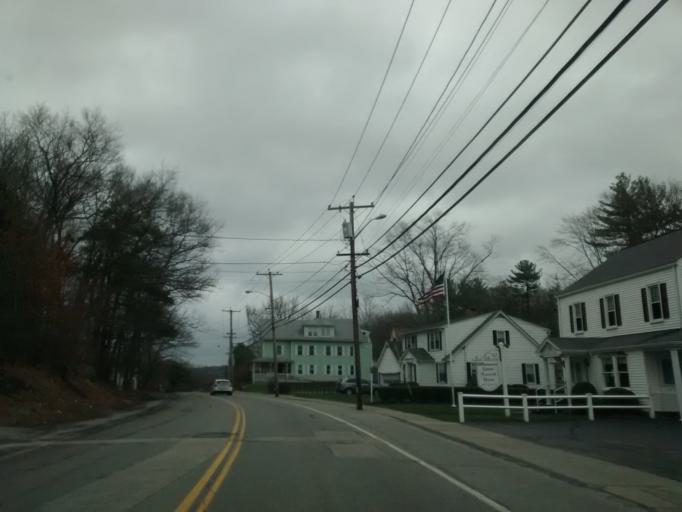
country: US
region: Massachusetts
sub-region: Worcester County
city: Whitinsville
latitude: 42.1186
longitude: -71.6511
